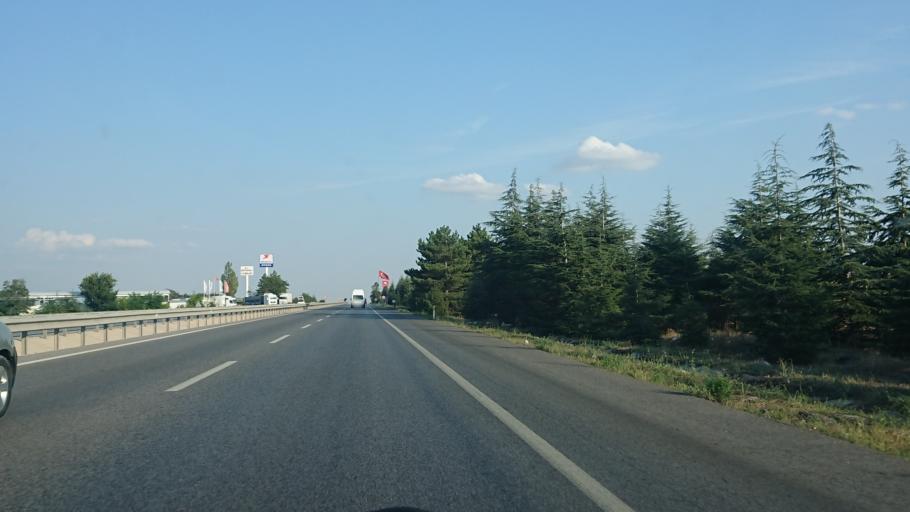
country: TR
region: Eskisehir
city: Mahmudiye
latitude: 39.5883
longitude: 30.8952
